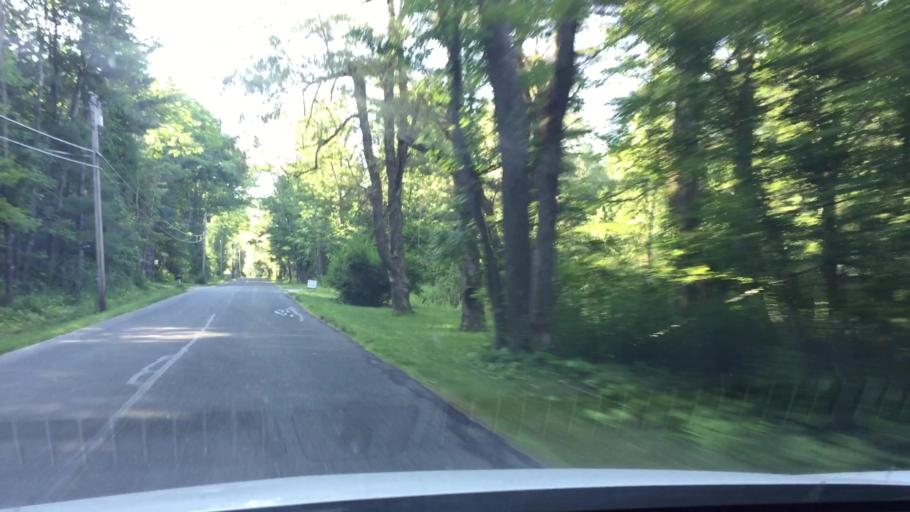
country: US
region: Massachusetts
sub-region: Berkshire County
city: Lee
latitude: 42.2750
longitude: -73.2054
